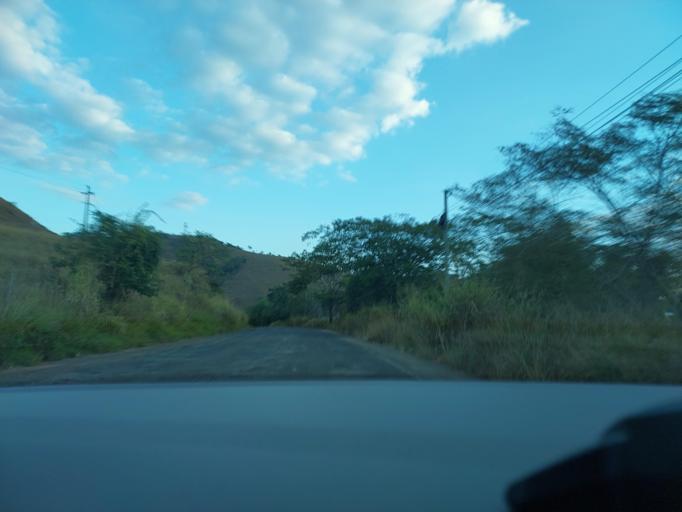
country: BR
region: Rio de Janeiro
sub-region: Natividade
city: Natividade
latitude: -21.1941
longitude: -42.1166
